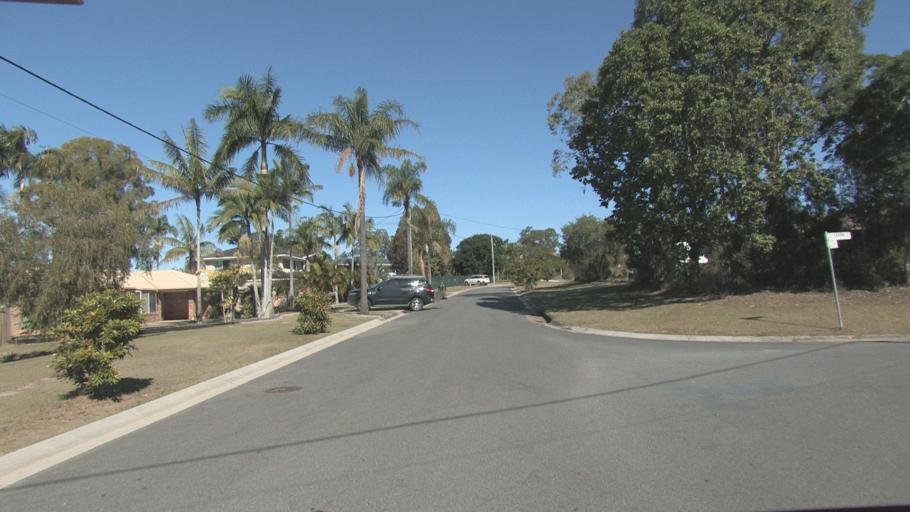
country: AU
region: Queensland
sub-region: Logan
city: Logan Reserve
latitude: -27.6848
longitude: 153.0635
